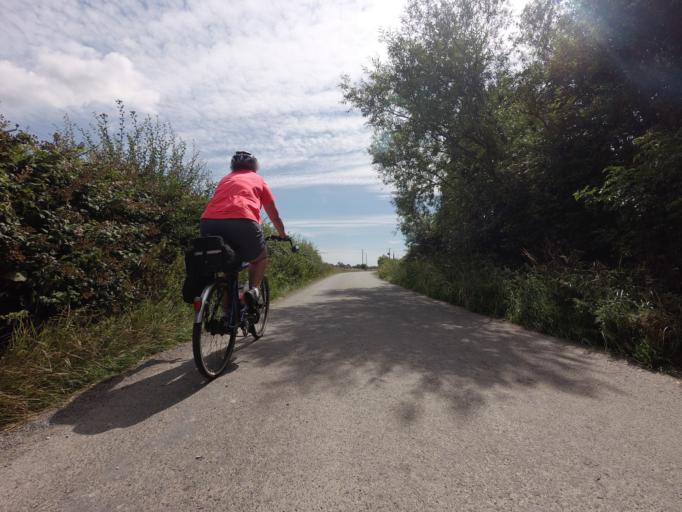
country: GB
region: England
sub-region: Kent
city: Stone
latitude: 51.0063
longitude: 0.7960
